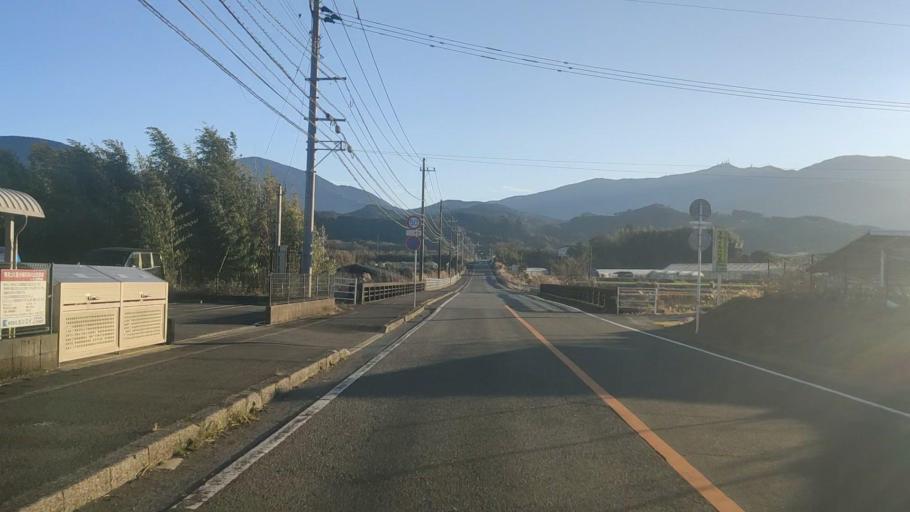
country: JP
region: Miyazaki
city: Miyazaki-shi
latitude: 31.8287
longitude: 131.2988
